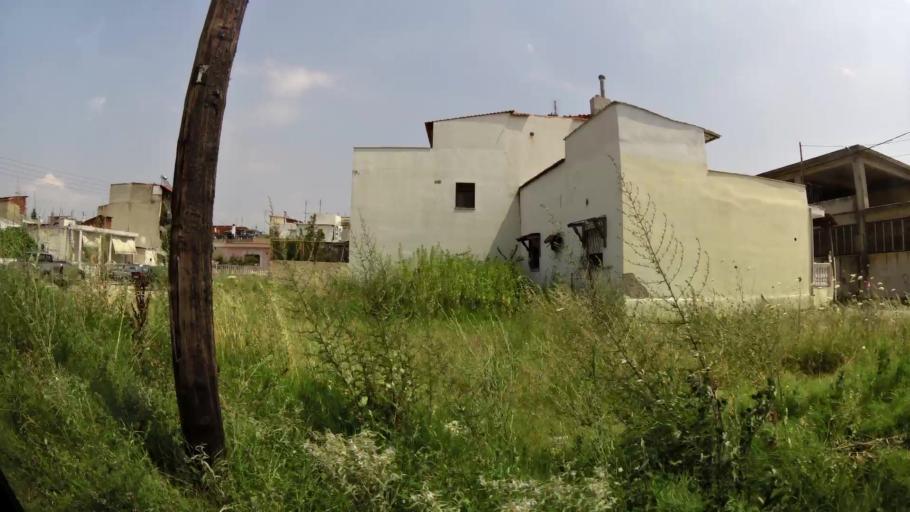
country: GR
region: Central Macedonia
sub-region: Nomos Thessalonikis
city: Menemeni
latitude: 40.6595
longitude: 22.8953
